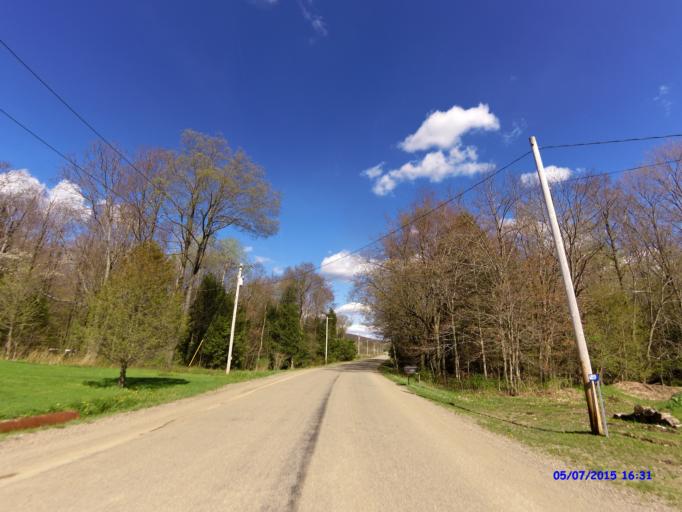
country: US
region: New York
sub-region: Cattaraugus County
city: Little Valley
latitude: 42.3278
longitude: -78.6912
